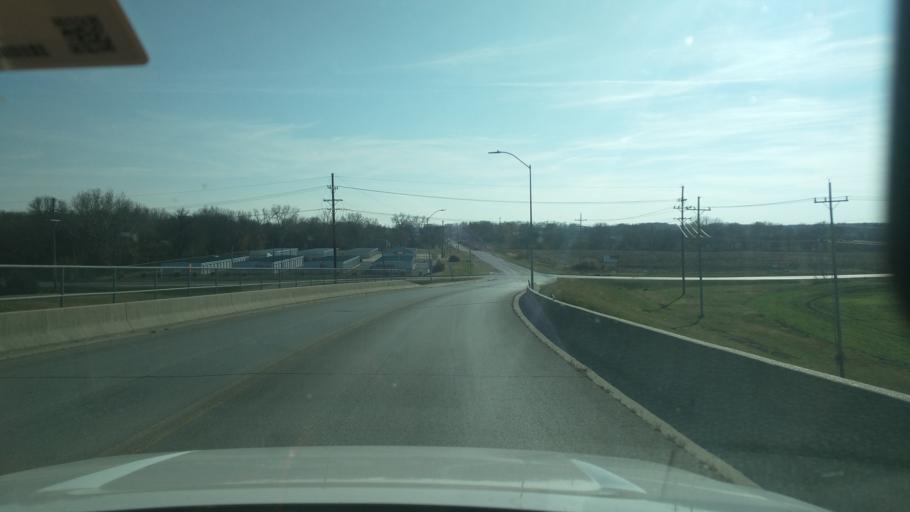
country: US
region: Kansas
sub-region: Lyon County
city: Emporia
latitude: 38.3992
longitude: -96.2077
